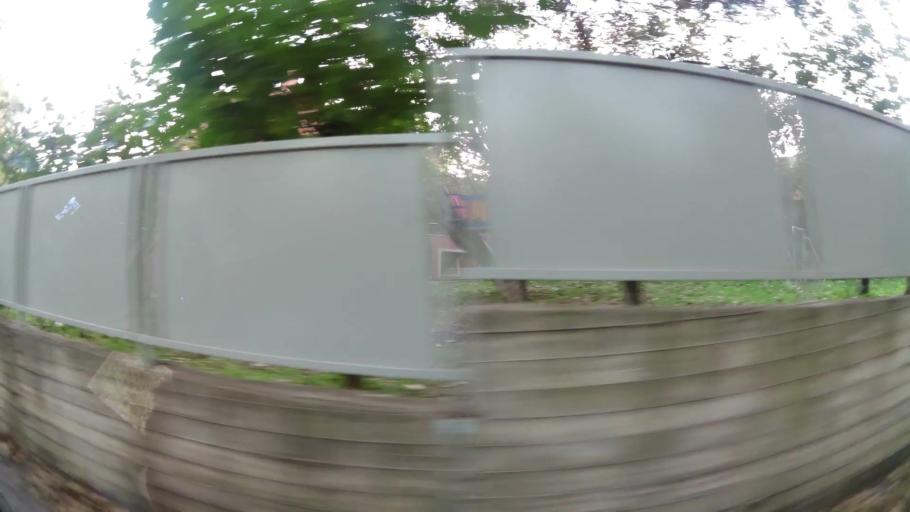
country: GR
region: Attica
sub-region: Nomarchia Anatolikis Attikis
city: Kryoneri
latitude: 38.1424
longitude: 23.8358
